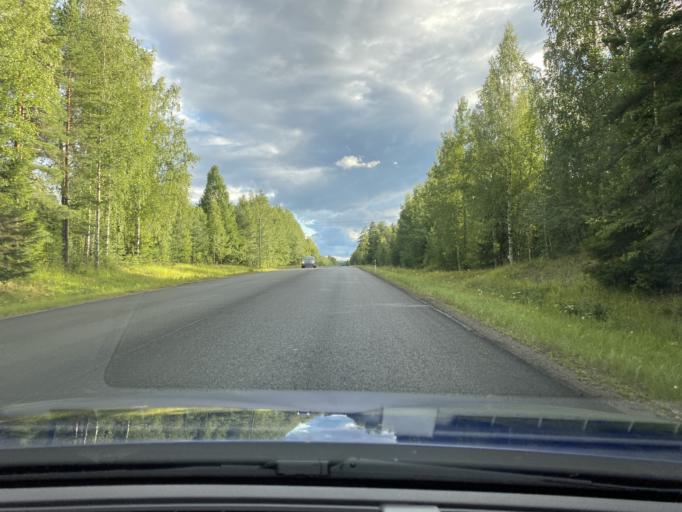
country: FI
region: Haeme
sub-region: Haemeenlinna
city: Renko
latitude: 60.9368
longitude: 24.3741
